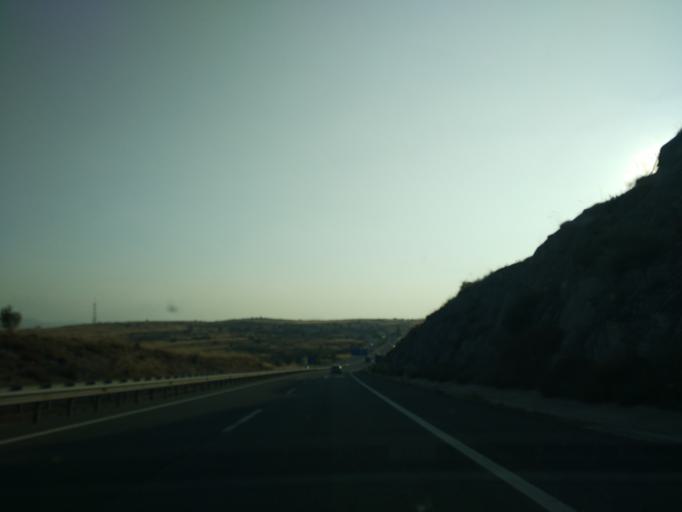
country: ES
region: Castille and Leon
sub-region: Provincia de Avila
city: Avila
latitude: 40.6725
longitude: -4.7044
